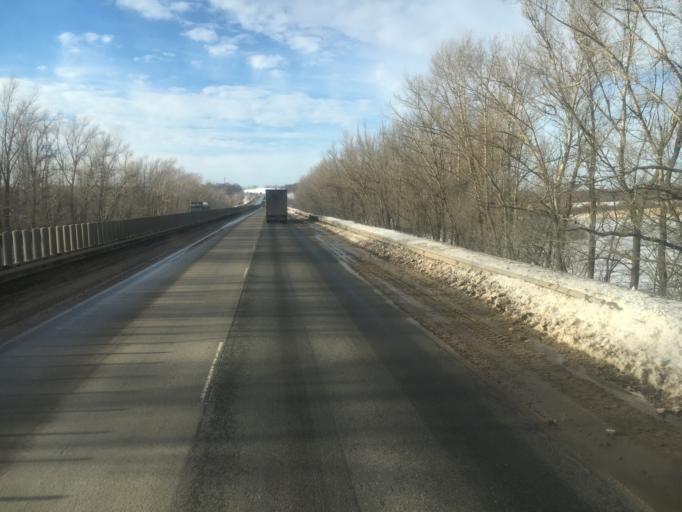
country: RU
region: Samara
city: Mirnyy
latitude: 53.4404
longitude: 50.2773
